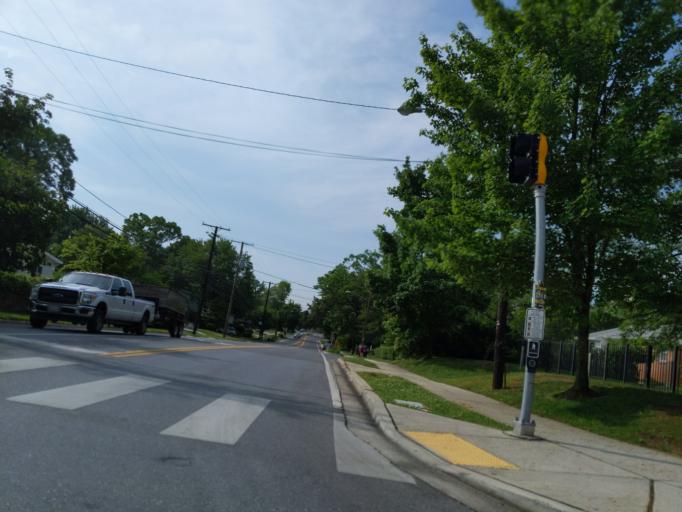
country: US
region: Maryland
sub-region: Montgomery County
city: Kemp Mill
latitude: 39.0411
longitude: -77.0291
